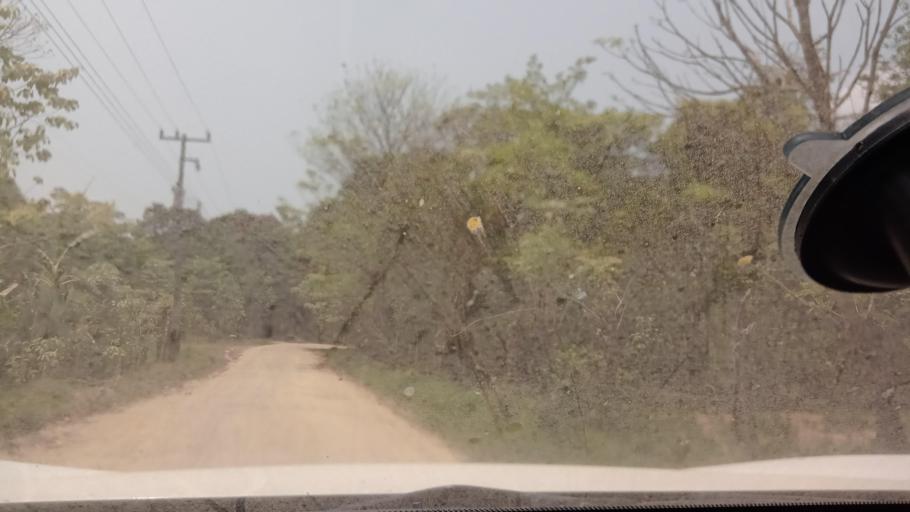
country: MX
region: Chiapas
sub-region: Tecpatan
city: Raudales Malpaso
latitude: 17.4564
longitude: -93.7974
